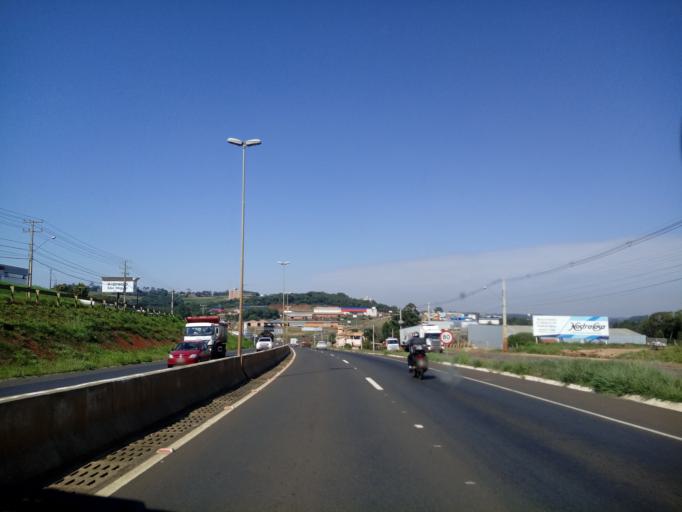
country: BR
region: Santa Catarina
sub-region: Chapeco
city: Chapeco
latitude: -27.0449
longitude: -52.6362
